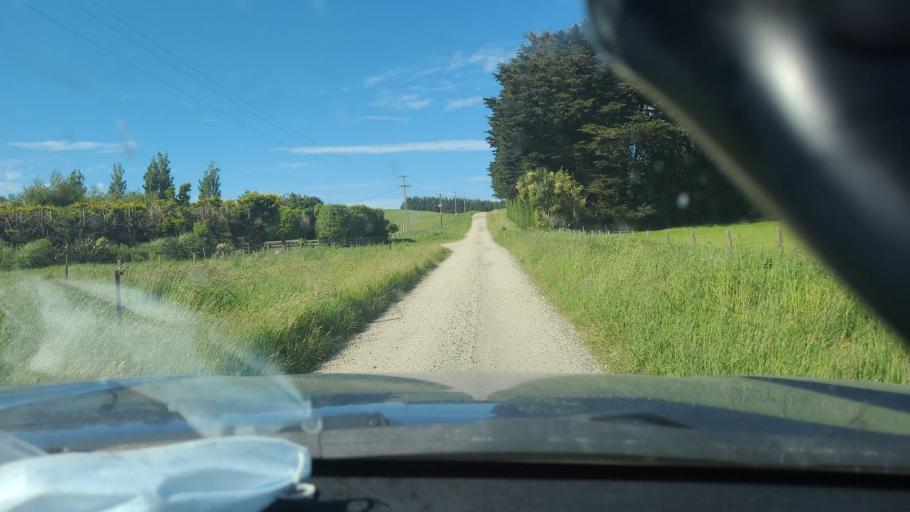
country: NZ
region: Southland
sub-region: Gore District
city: Gore
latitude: -46.5071
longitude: 168.8150
